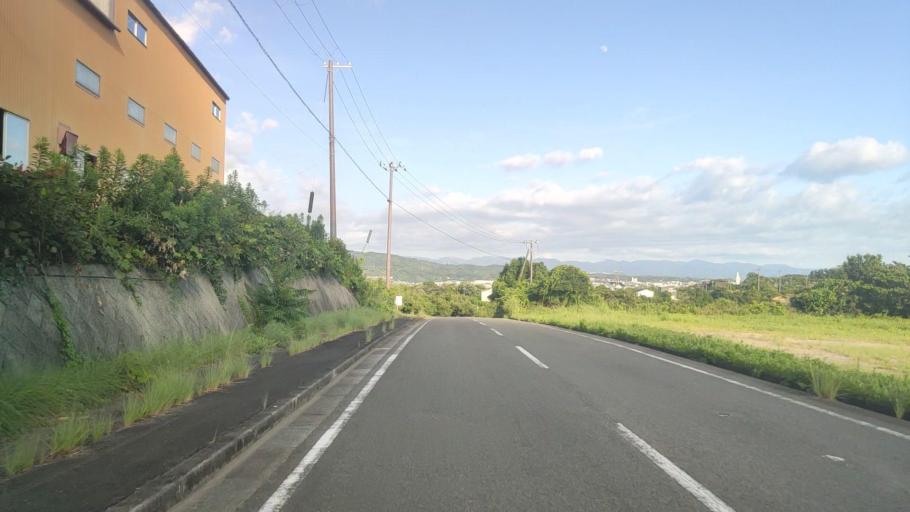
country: JP
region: Wakayama
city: Tanabe
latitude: 33.7777
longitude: 135.3023
